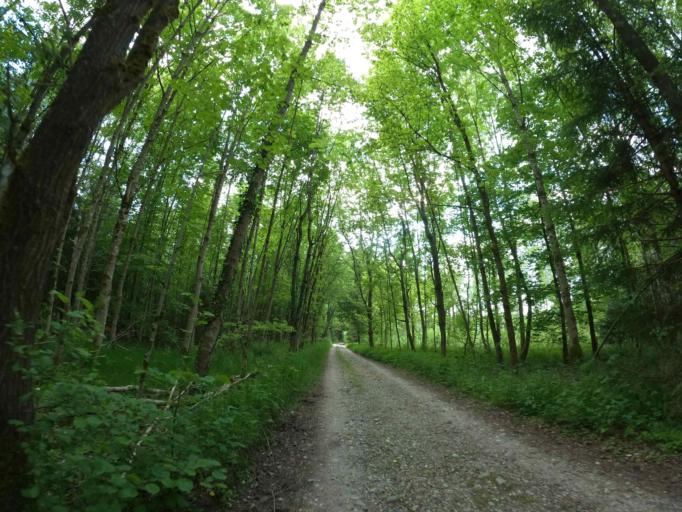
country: DE
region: Bavaria
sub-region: Upper Bavaria
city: Sauerlach
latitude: 47.9887
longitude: 11.6403
